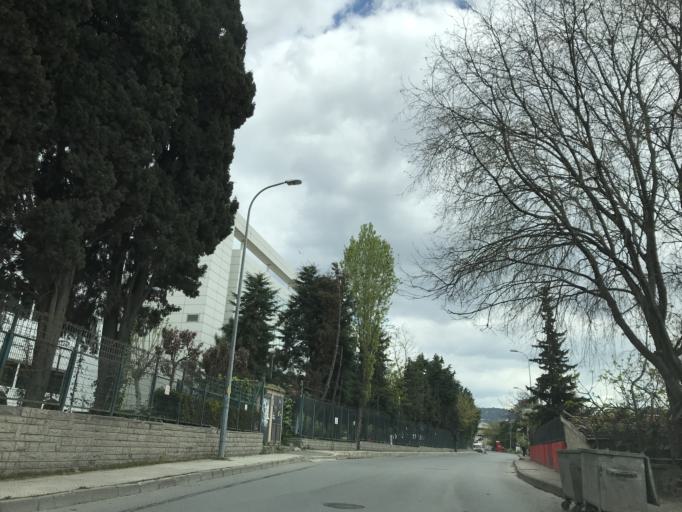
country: TR
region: Istanbul
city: Maltepe
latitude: 40.8994
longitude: 29.2032
